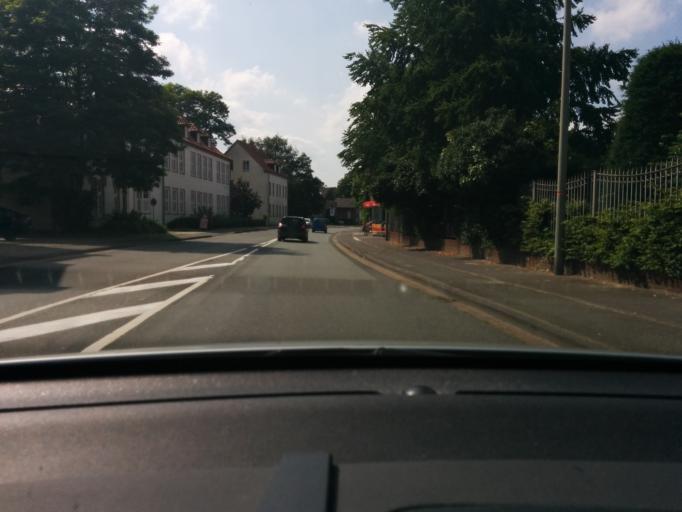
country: DE
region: North Rhine-Westphalia
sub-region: Regierungsbezirk Munster
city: Ochtrup
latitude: 52.1973
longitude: 7.2377
